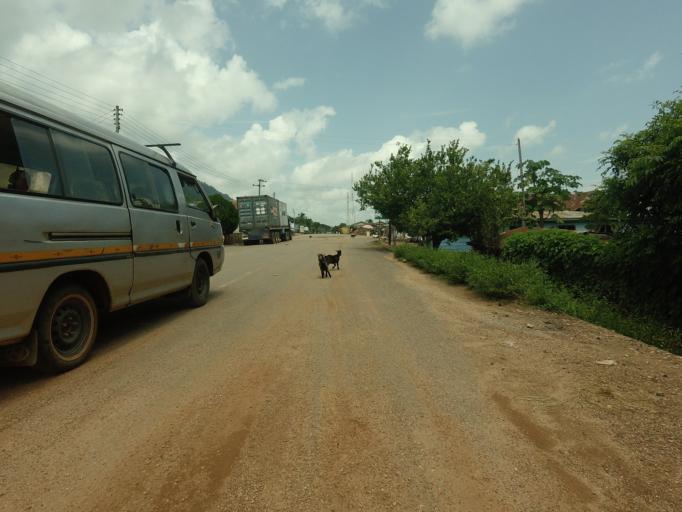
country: GH
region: Volta
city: Ho
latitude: 6.7610
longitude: 0.3623
